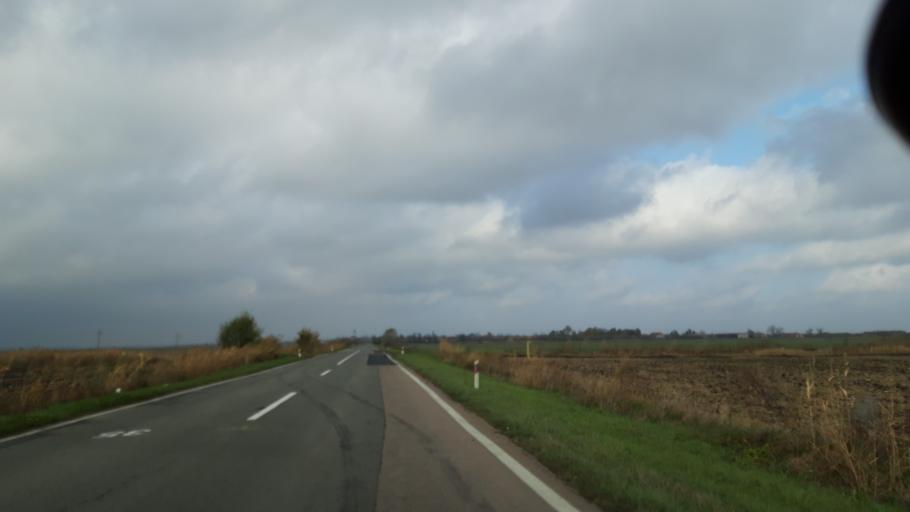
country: RS
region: Autonomna Pokrajina Vojvodina
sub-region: Severnobanatski Okrug
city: Coka
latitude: 45.9166
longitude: 20.1497
